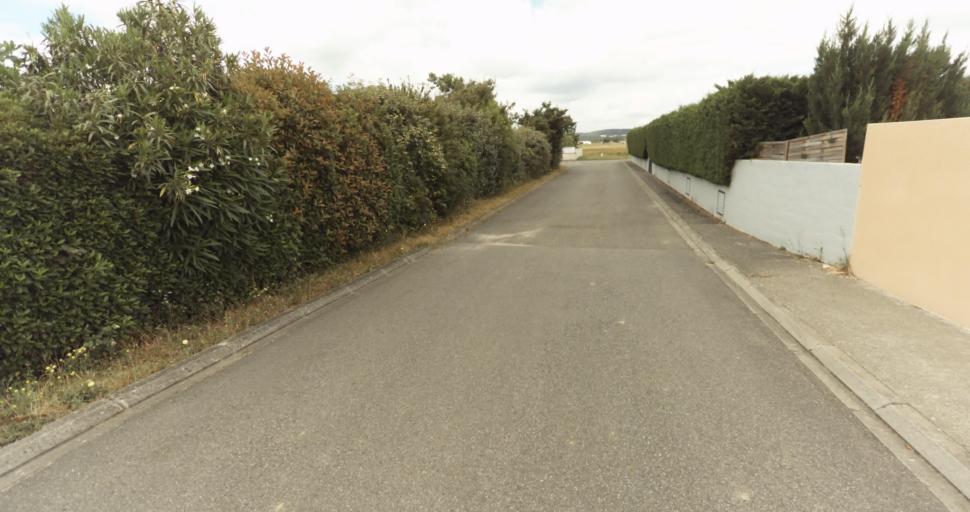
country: FR
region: Midi-Pyrenees
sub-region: Departement de la Haute-Garonne
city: Fontenilles
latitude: 43.5576
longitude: 1.1967
